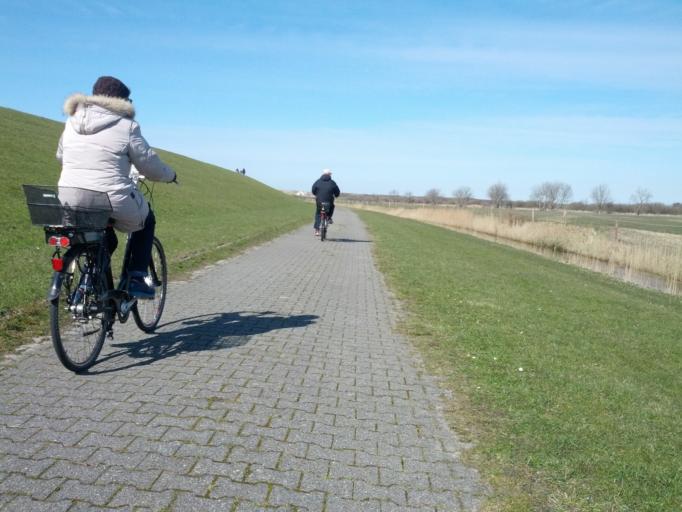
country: DE
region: Lower Saxony
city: Langeoog
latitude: 53.7298
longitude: 7.4824
